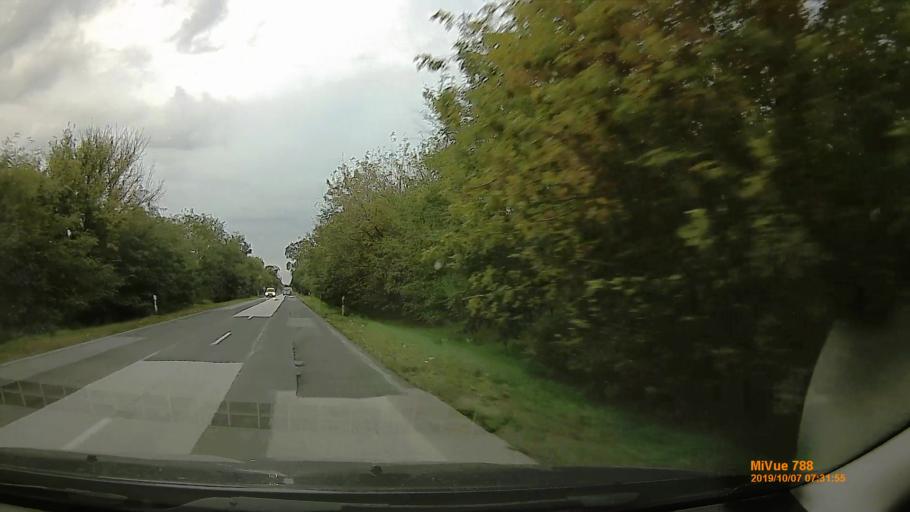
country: HU
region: Bacs-Kiskun
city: Nyarlorinc
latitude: 46.8810
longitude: 19.8435
